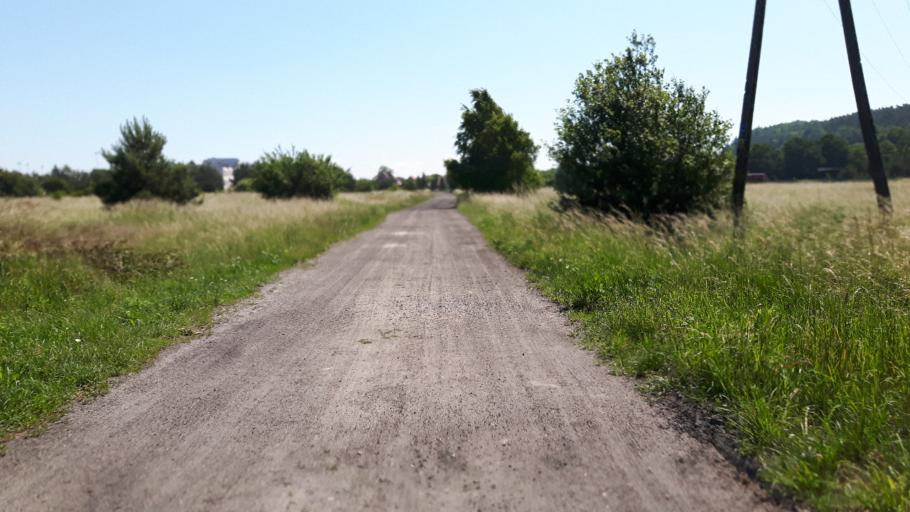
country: PL
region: Pomeranian Voivodeship
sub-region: Powiat slupski
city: Smoldzino
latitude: 54.6667
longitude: 17.2058
